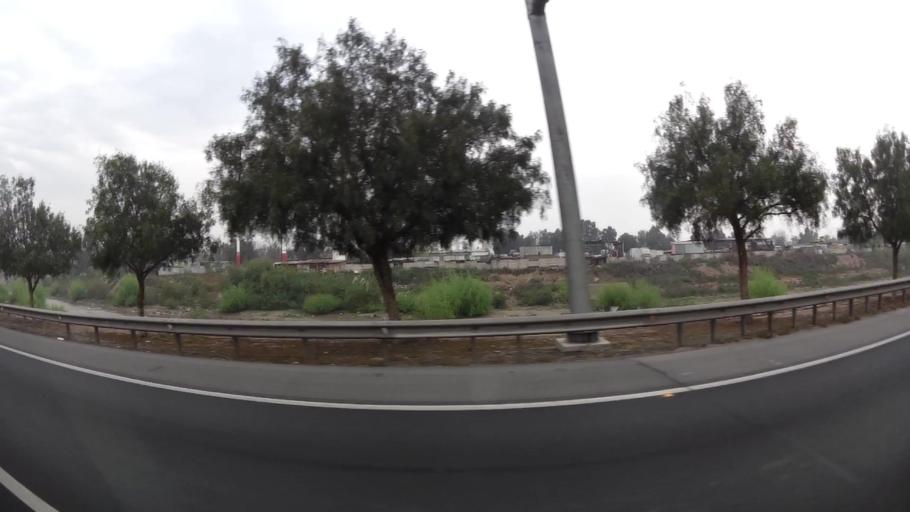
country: CL
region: Santiago Metropolitan
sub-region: Provincia de Santiago
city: Lo Prado
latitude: -33.4122
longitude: -70.7605
